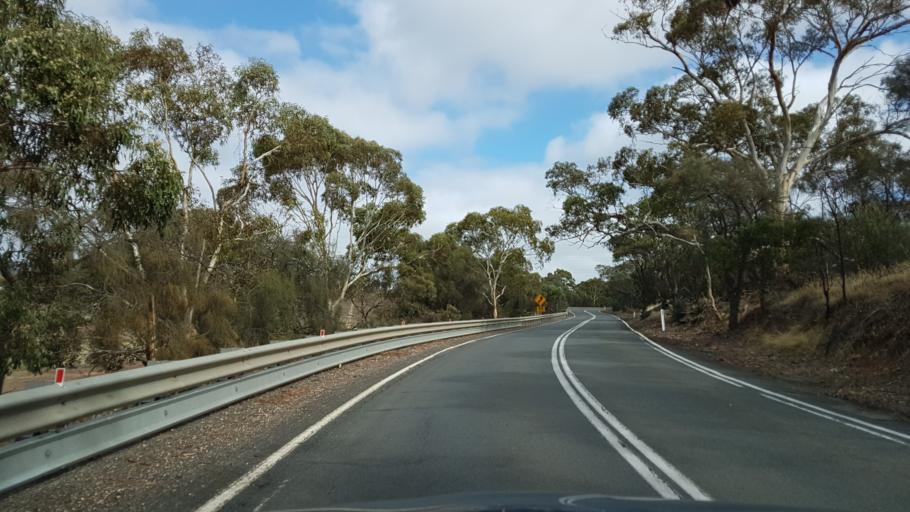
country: AU
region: South Australia
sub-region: Mount Barker
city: Callington
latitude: -35.0513
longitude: 139.0023
